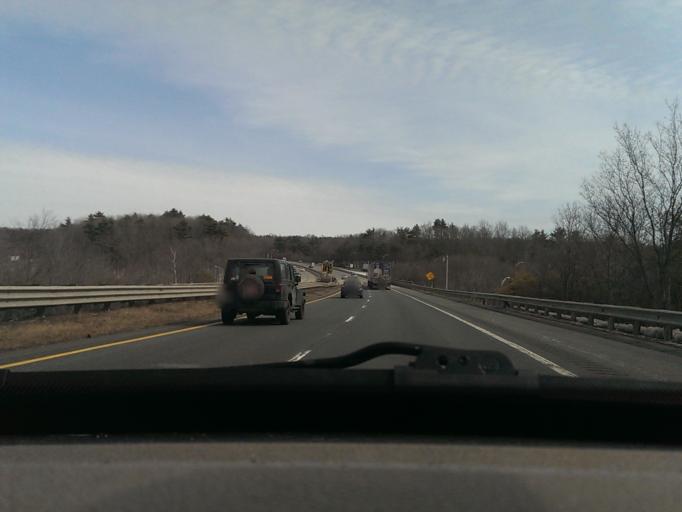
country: US
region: Massachusetts
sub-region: Worcester County
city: Sturbridge
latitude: 42.1295
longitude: -72.0652
